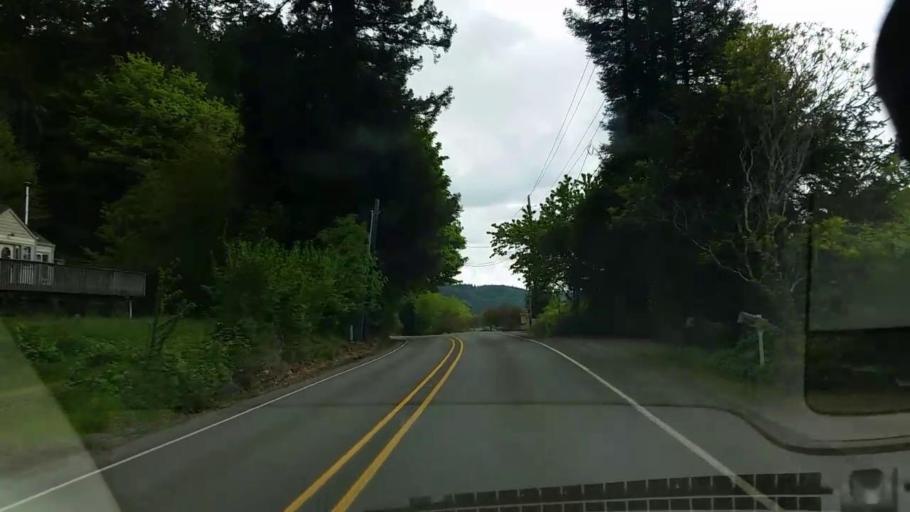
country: US
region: Washington
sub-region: Mason County
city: Shelton
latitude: 47.3477
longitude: -123.1082
